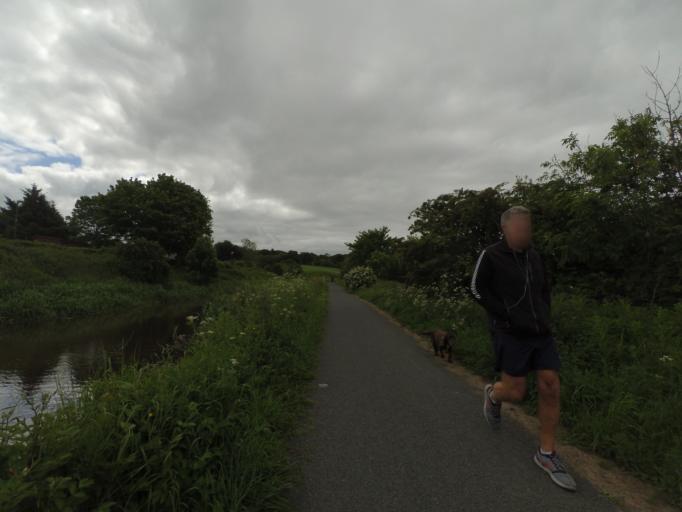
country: GB
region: Scotland
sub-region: West Lothian
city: Linlithgow
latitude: 55.9698
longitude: -3.6119
